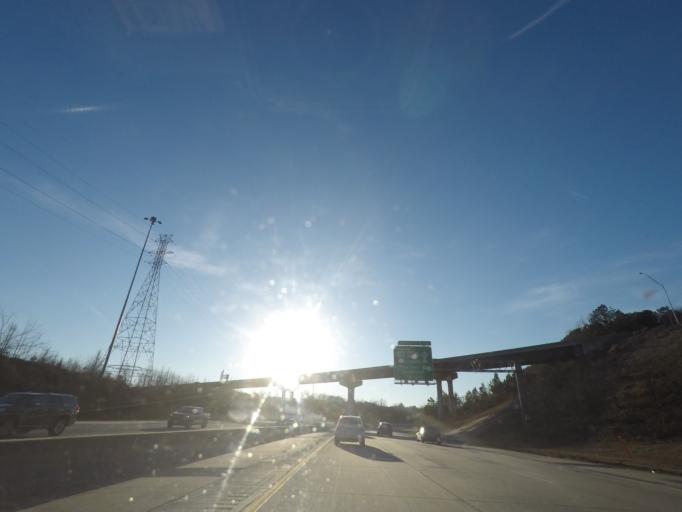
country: US
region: North Carolina
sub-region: Durham County
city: Durham
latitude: 36.0144
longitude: -78.8689
